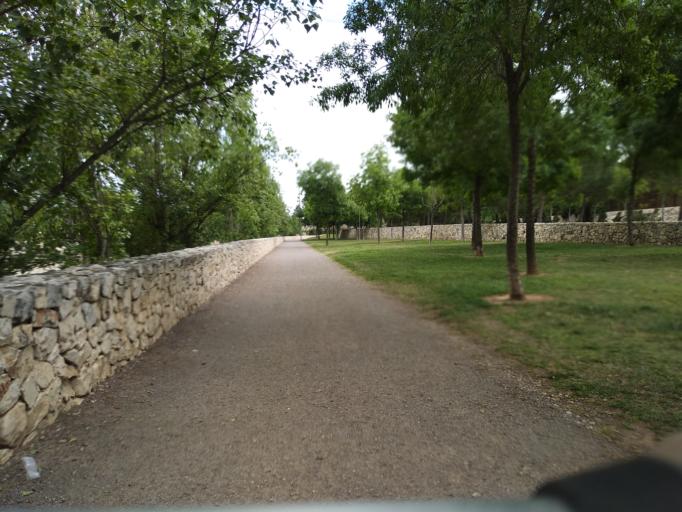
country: ES
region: Valencia
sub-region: Provincia de Valencia
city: Mislata
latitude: 39.4812
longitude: -0.4105
